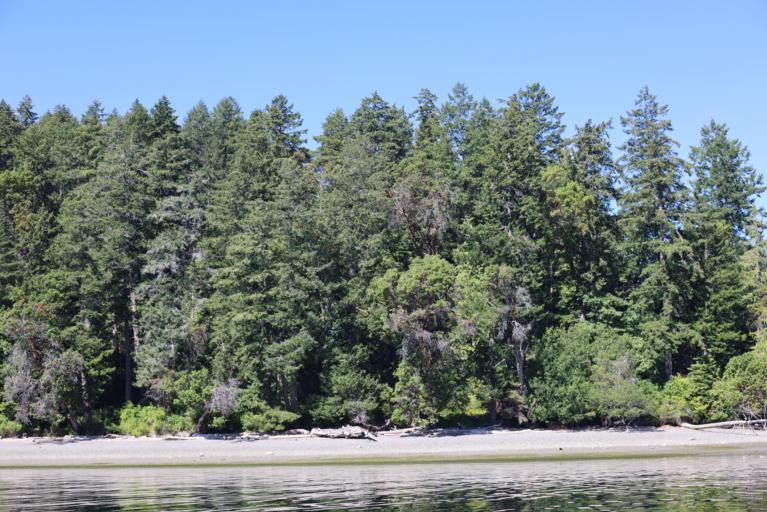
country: CA
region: British Columbia
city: North Cowichan
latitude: 48.8585
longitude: -123.6159
